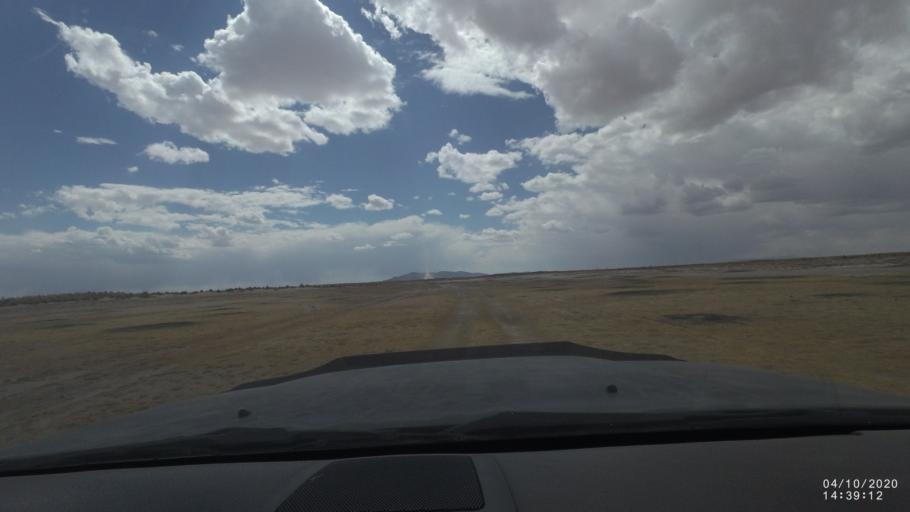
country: BO
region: Oruro
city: Poopo
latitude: -18.6783
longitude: -67.4844
